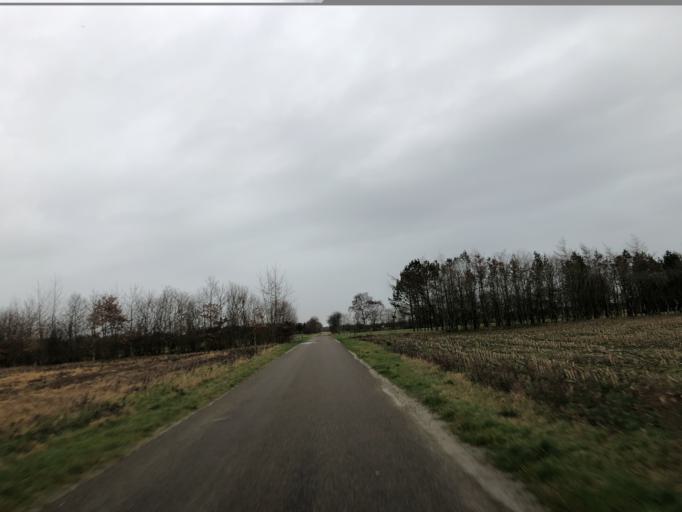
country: DK
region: Central Jutland
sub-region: Holstebro Kommune
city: Vinderup
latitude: 56.3765
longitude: 8.8511
